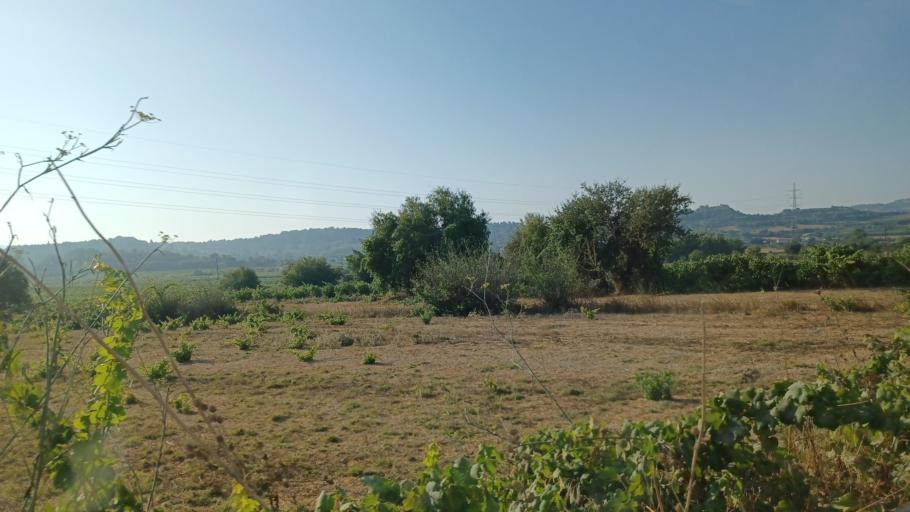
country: CY
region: Pafos
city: Tala
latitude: 34.8896
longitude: 32.4907
